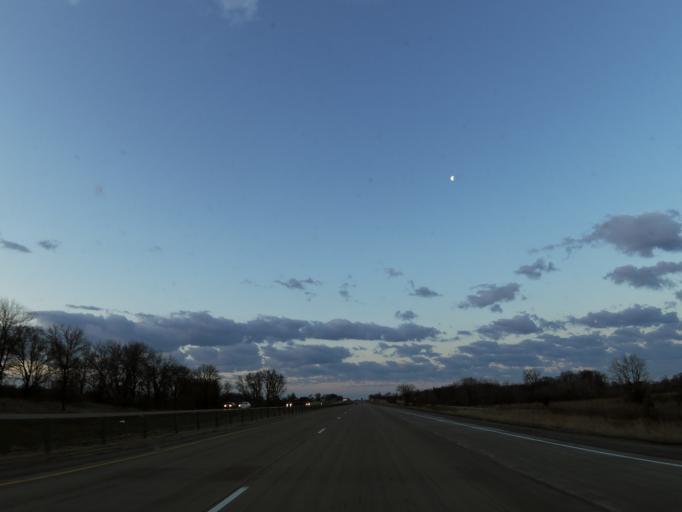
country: US
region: Minnesota
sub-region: Scott County
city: Elko New Market
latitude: 44.5692
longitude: -93.2987
